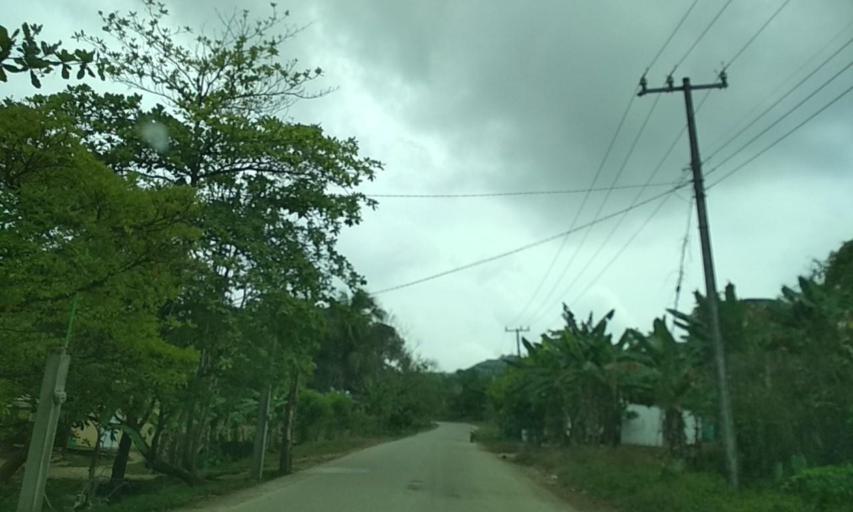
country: MX
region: Veracruz
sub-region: Uxpanapa
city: Poblado 10
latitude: 17.4780
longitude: -94.1195
